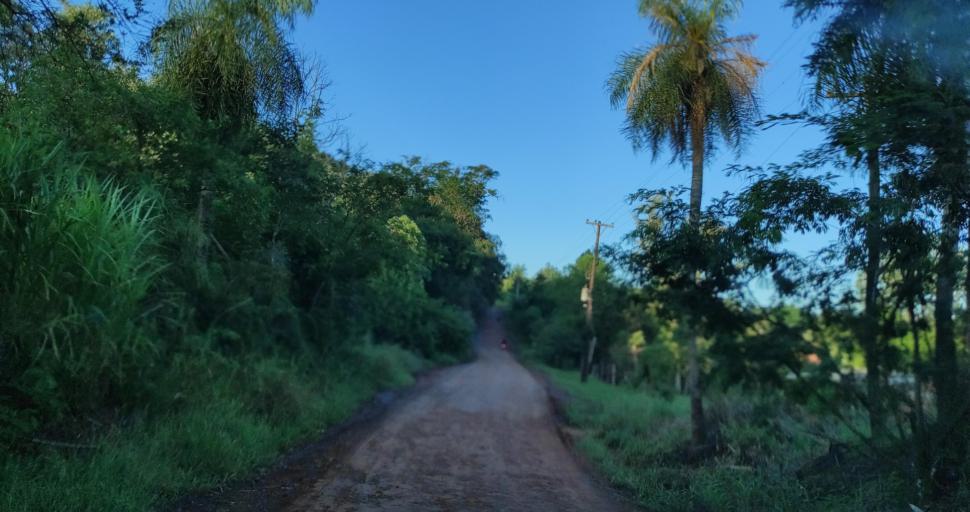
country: AR
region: Misiones
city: Gobernador Roca
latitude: -27.2195
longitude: -55.4259
